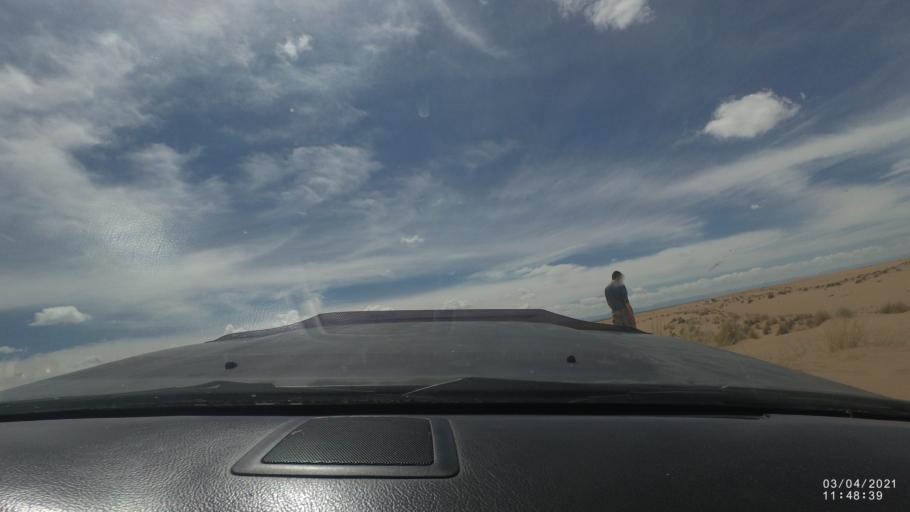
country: BO
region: Oruro
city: Poopo
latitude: -18.7011
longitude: -67.5037
